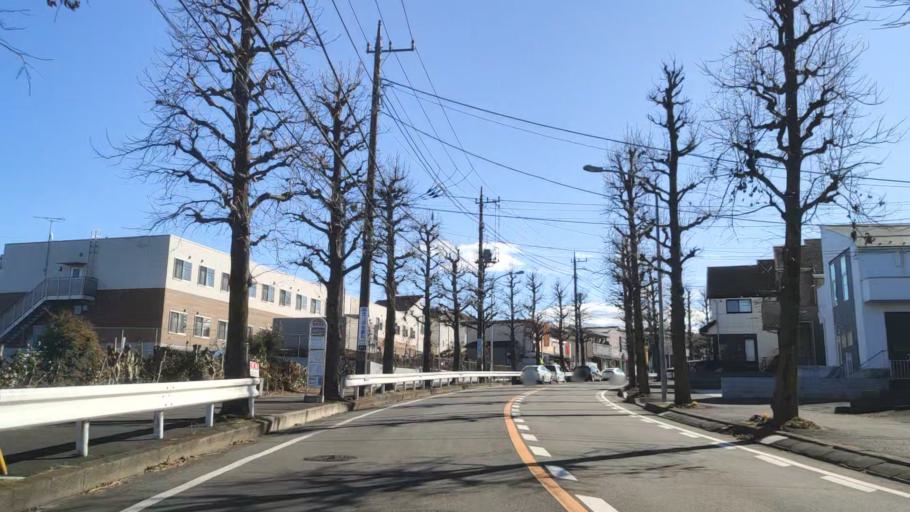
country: JP
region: Tokyo
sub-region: Machida-shi
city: Machida
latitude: 35.5188
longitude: 139.5081
